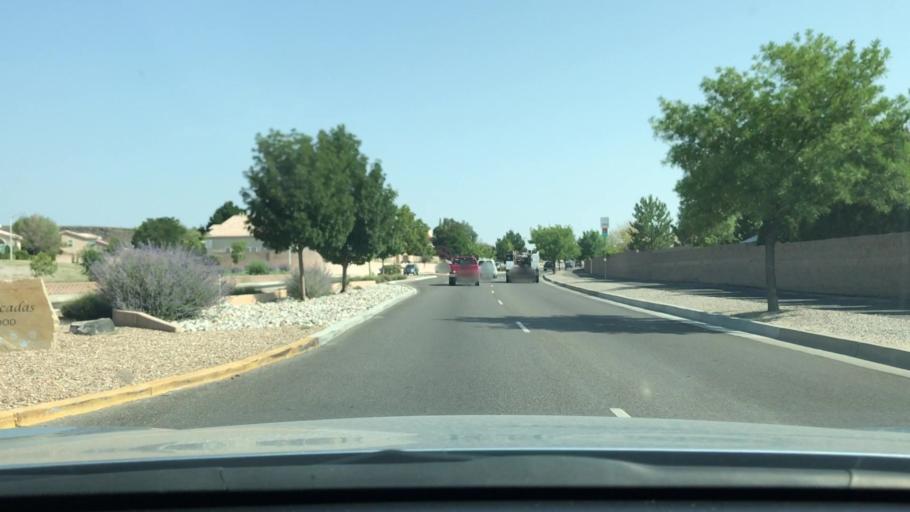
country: US
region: New Mexico
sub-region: Bernalillo County
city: Paradise Hills
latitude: 35.1826
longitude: -106.6871
